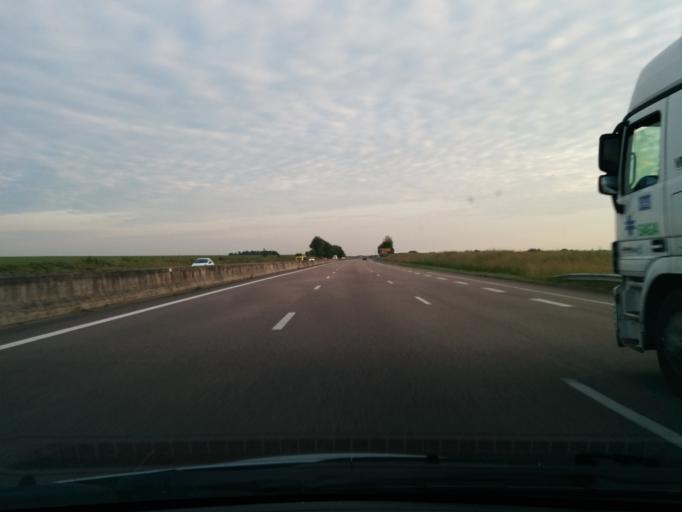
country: FR
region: Haute-Normandie
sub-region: Departement de l'Eure
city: Saint-Aubin-sur-Gaillon
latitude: 49.1099
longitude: 1.3394
